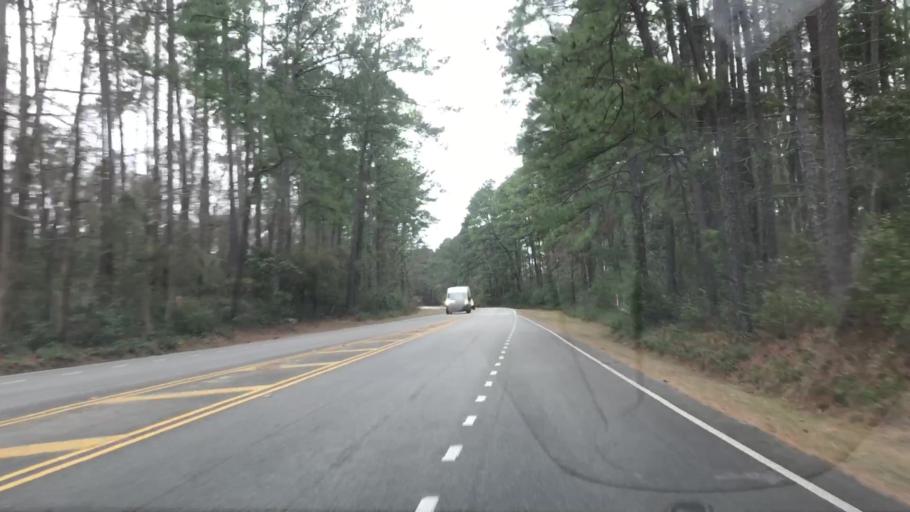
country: US
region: South Carolina
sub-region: Horry County
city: Red Hill
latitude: 33.7815
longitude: -78.9915
